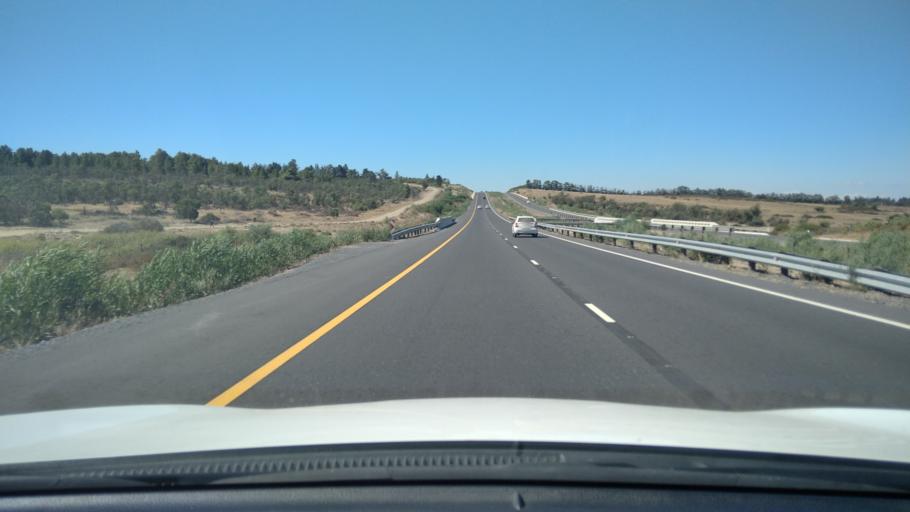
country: ZA
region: Western Cape
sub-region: City of Cape Town
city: Atlantis
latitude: -33.6178
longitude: 18.5894
